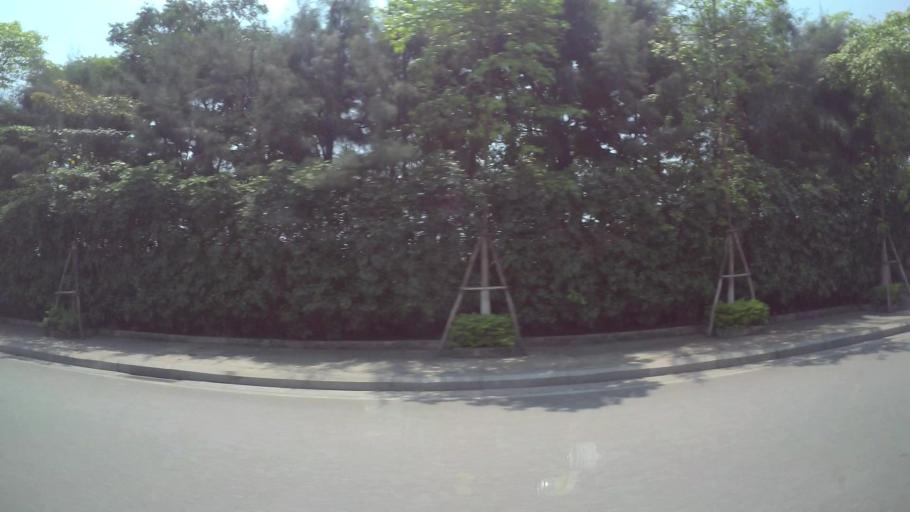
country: VN
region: Ha Noi
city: Trau Quy
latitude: 21.0340
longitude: 105.8967
